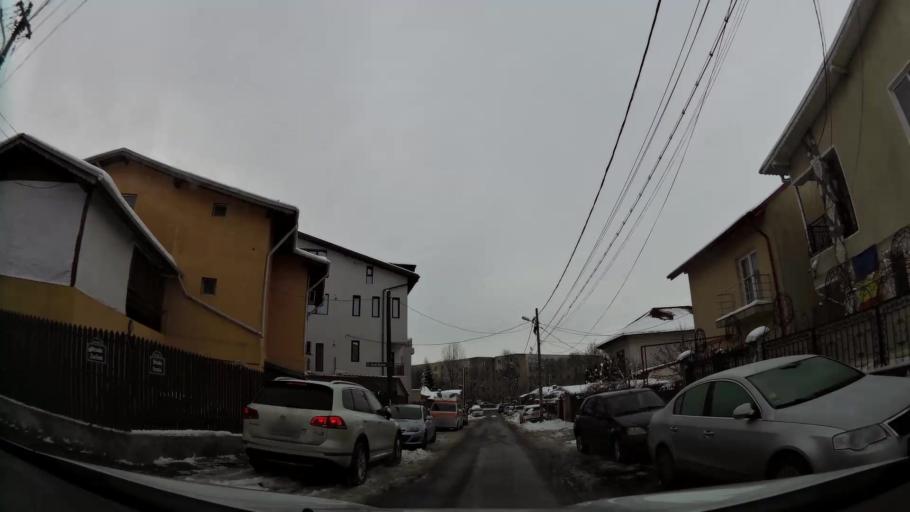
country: RO
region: Bucuresti
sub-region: Municipiul Bucuresti
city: Bucuresti
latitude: 44.3895
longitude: 26.0999
